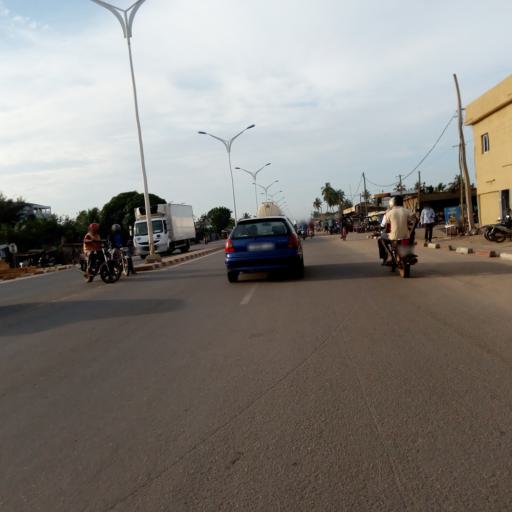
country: TG
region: Maritime
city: Lome
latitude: 6.1632
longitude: 1.2839
